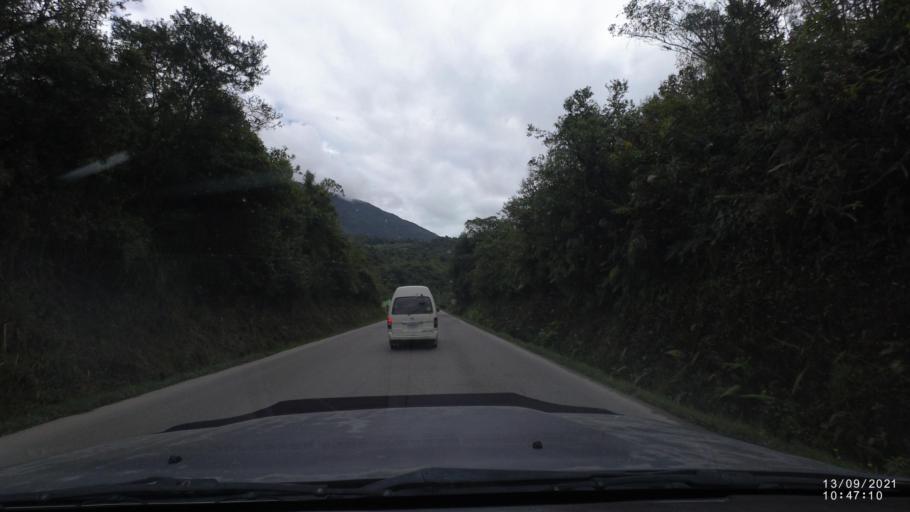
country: BO
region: Cochabamba
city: Colomi
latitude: -17.2014
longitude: -65.8629
